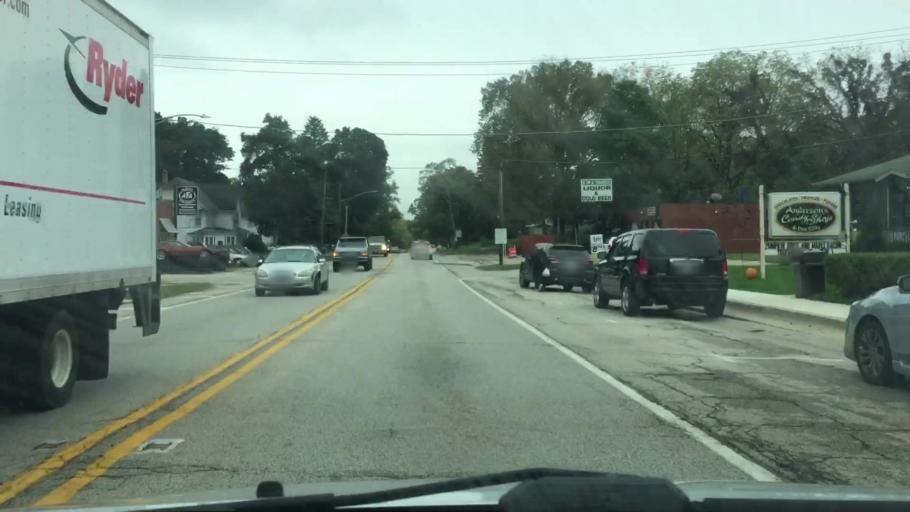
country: US
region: Illinois
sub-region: McHenry County
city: Richmond
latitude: 42.4754
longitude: -88.3062
